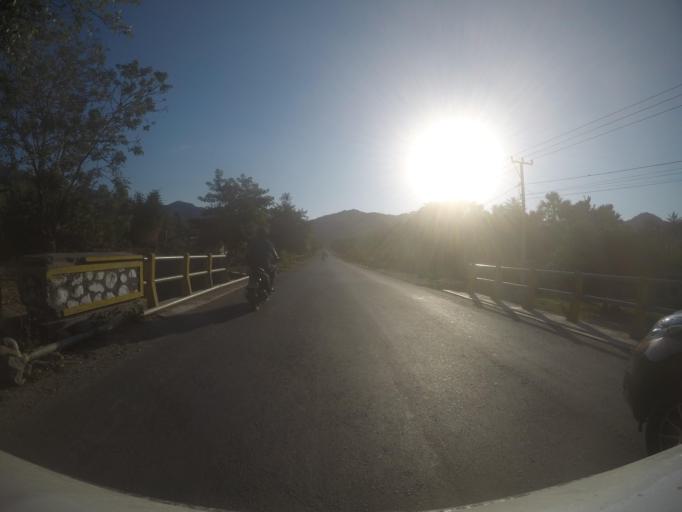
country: TL
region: Dili
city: Dili
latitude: -8.5558
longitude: 125.6530
